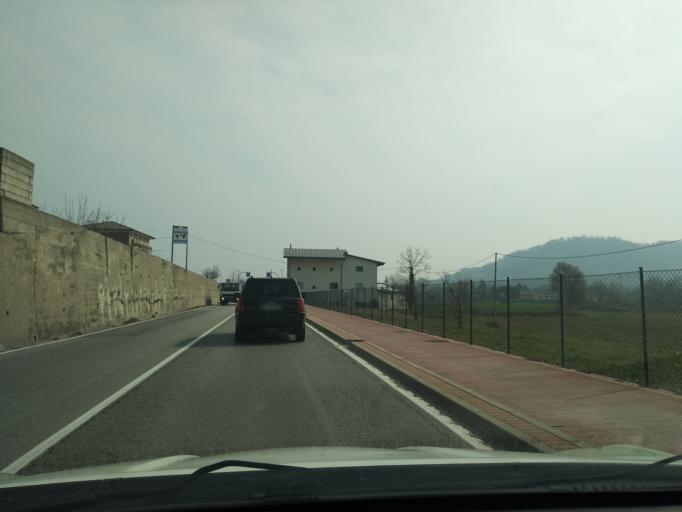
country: IT
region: Veneto
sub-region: Provincia di Vicenza
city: Arzignano
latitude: 45.5285
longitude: 11.3147
